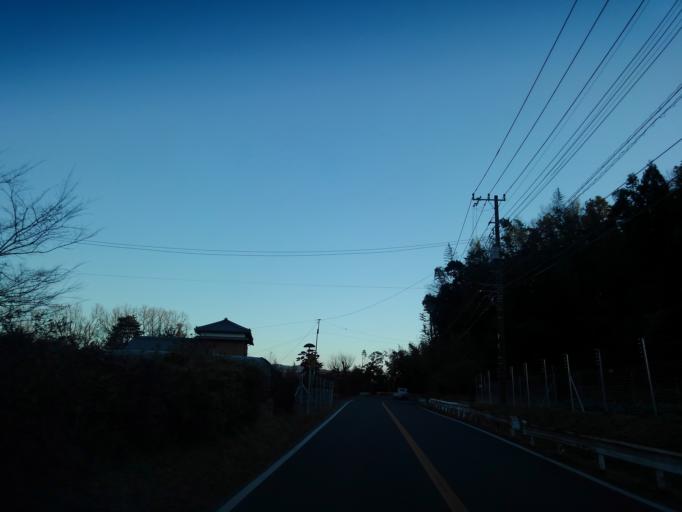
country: JP
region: Chiba
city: Kimitsu
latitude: 35.2970
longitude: 139.9797
